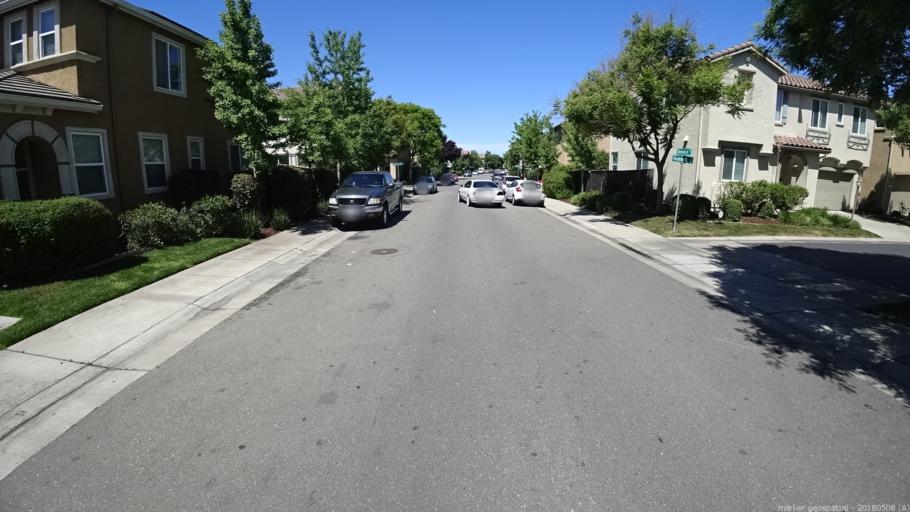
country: US
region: California
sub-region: Sacramento County
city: Elverta
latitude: 38.6750
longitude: -121.5363
